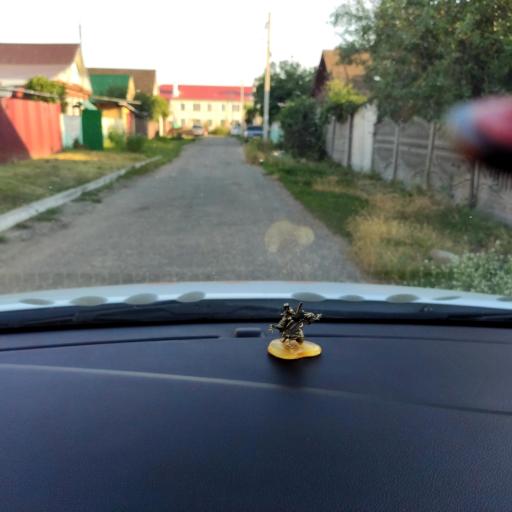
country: RU
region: Tatarstan
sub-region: Zelenodol'skiy Rayon
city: Zelenodolsk
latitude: 55.8478
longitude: 48.5515
